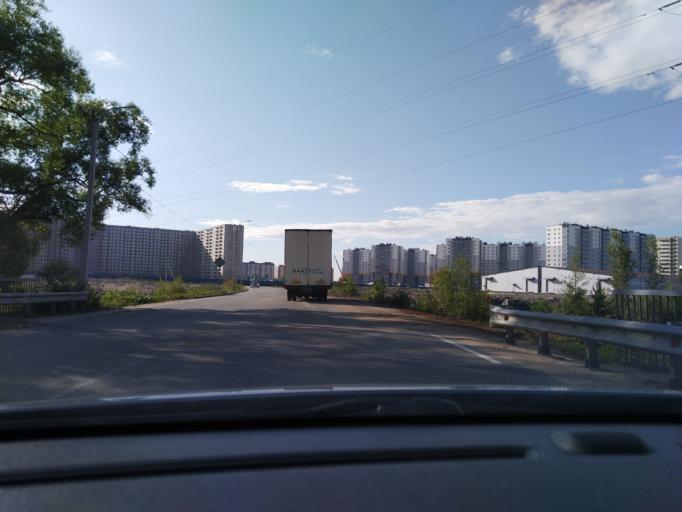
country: RU
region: St.-Petersburg
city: Gorelovo
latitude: 59.7846
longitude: 30.1687
